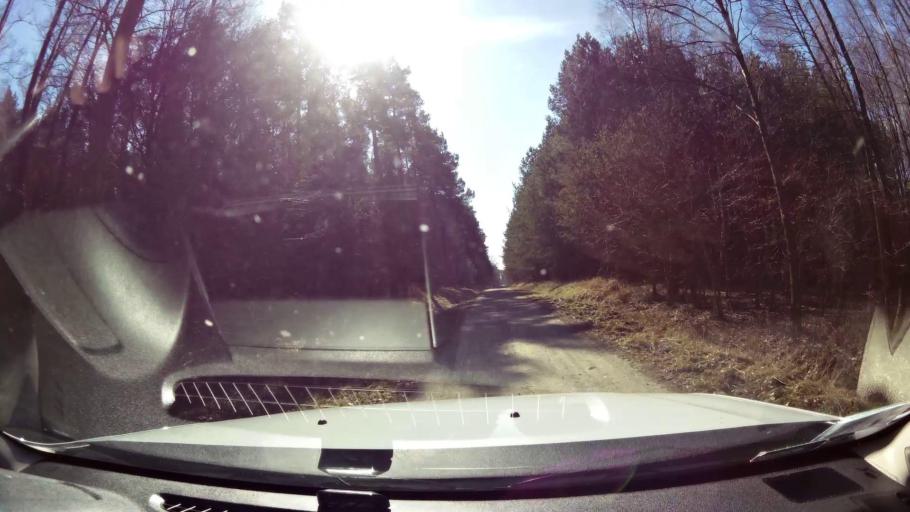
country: PL
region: West Pomeranian Voivodeship
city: Trzcinsko Zdroj
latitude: 53.0075
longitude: 14.6147
